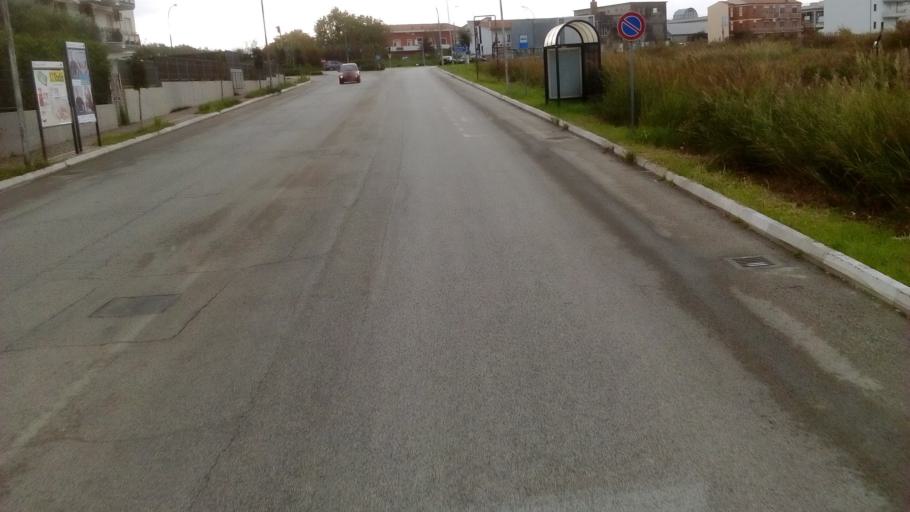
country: IT
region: Abruzzo
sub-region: Provincia di Chieti
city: Vasto
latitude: 42.1022
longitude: 14.7022
